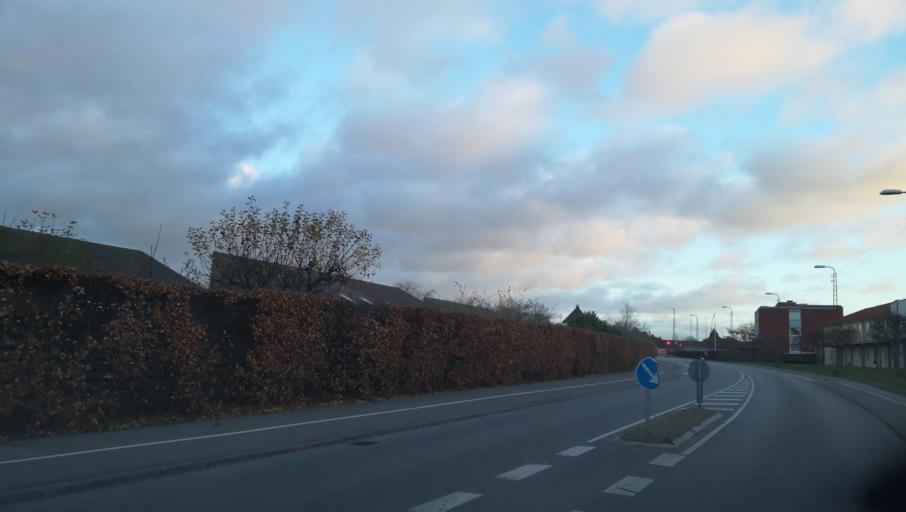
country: DK
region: Zealand
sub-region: Naestved Kommune
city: Naestved
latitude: 55.2294
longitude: 11.7474
